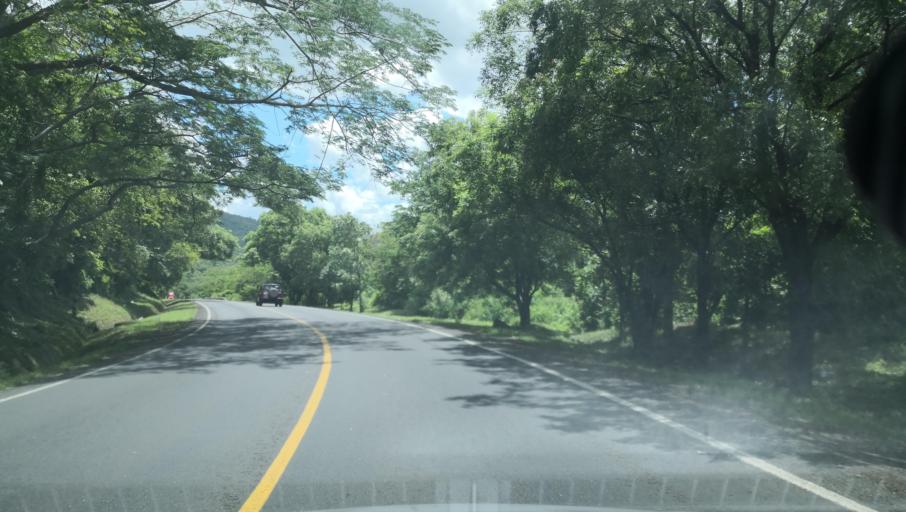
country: NI
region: Esteli
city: Condega
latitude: 13.3140
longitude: -86.3549
